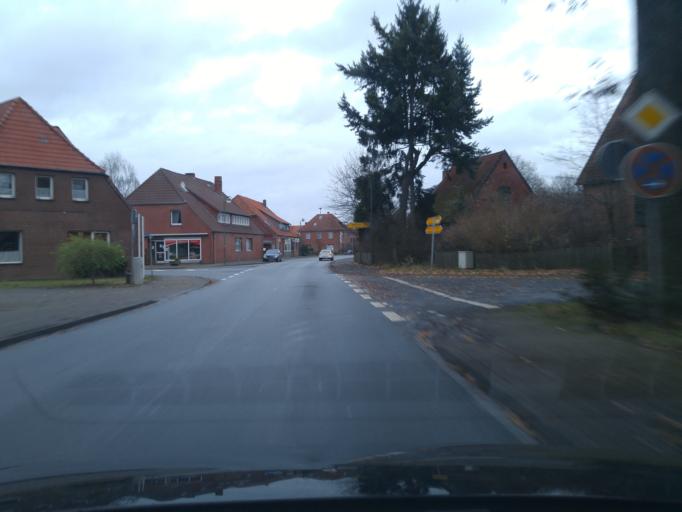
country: DE
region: Lower Saxony
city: Scharnebeck
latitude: 53.2932
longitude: 10.5075
